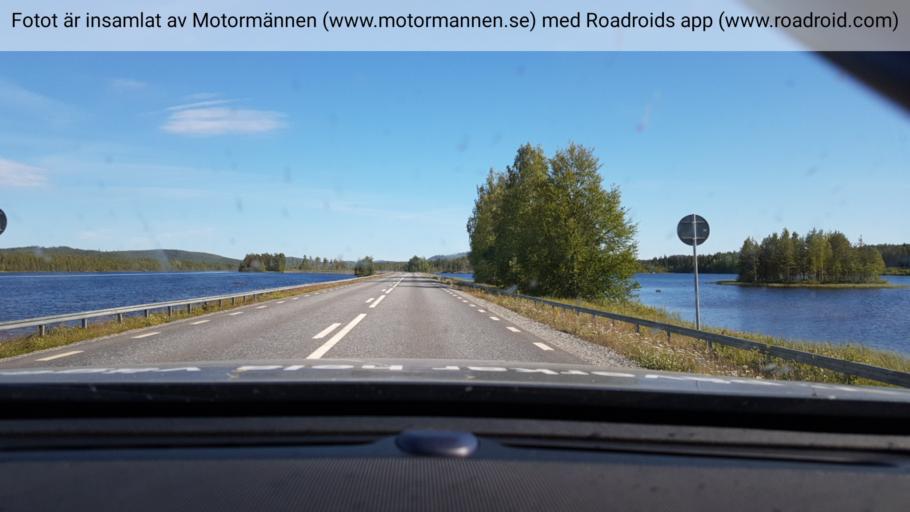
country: SE
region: Vaesterbotten
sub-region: Lycksele Kommun
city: Soderfors
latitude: 64.7572
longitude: 18.1685
